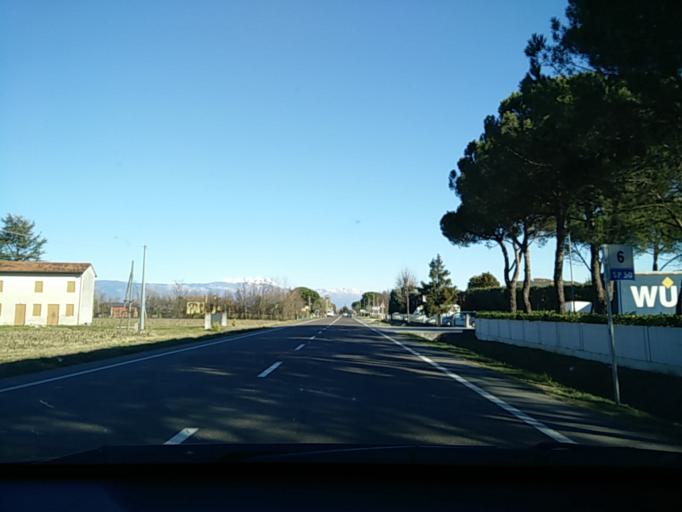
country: IT
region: Veneto
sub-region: Provincia di Treviso
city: Mansue
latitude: 45.8318
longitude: 12.5369
